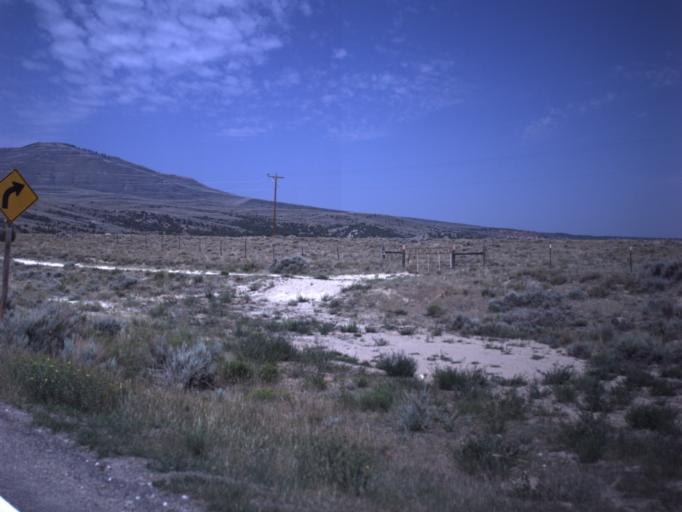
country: US
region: Utah
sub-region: Daggett County
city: Manila
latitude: 40.9765
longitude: -109.8244
